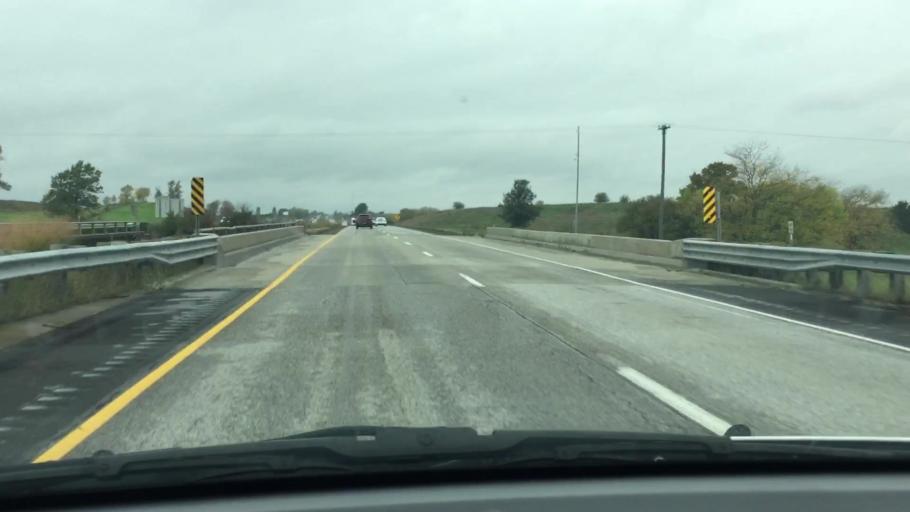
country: US
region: Iowa
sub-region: Johnson County
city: Tiffin
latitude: 41.6879
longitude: -91.8037
